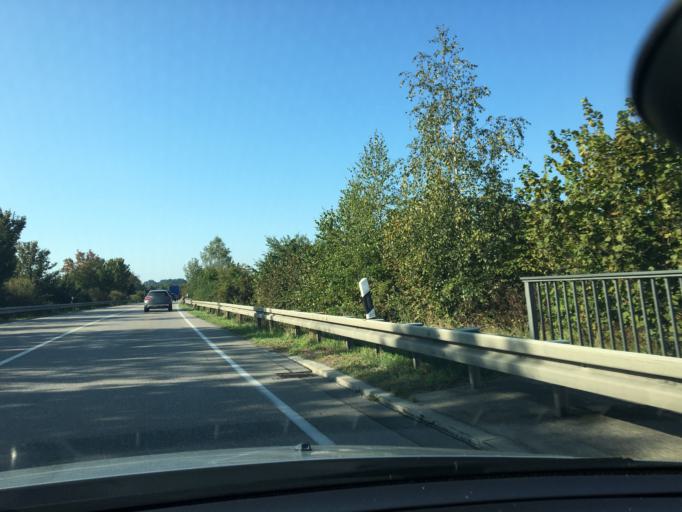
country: DE
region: Bavaria
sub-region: Upper Bavaria
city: Stammham
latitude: 48.3130
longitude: 11.8818
